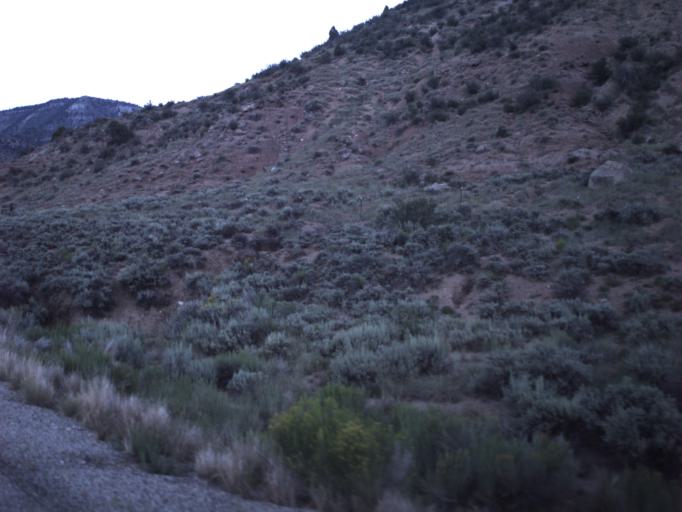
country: US
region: Utah
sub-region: Carbon County
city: Helper
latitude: 39.8281
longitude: -110.7883
